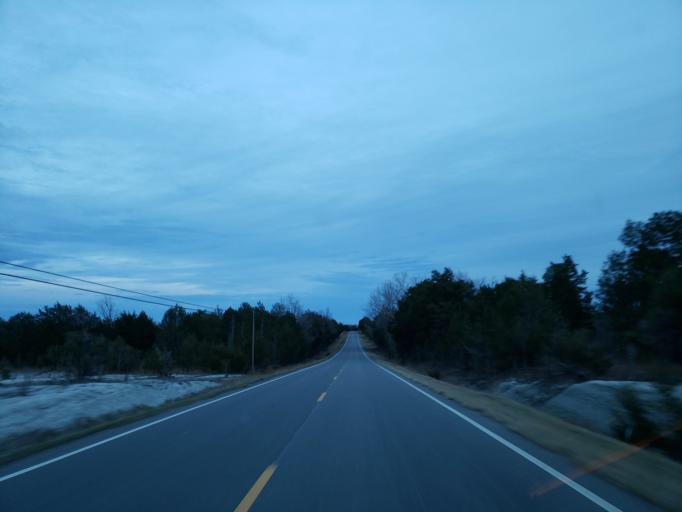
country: US
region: Alabama
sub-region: Sumter County
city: Livingston
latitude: 32.8097
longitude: -88.2225
